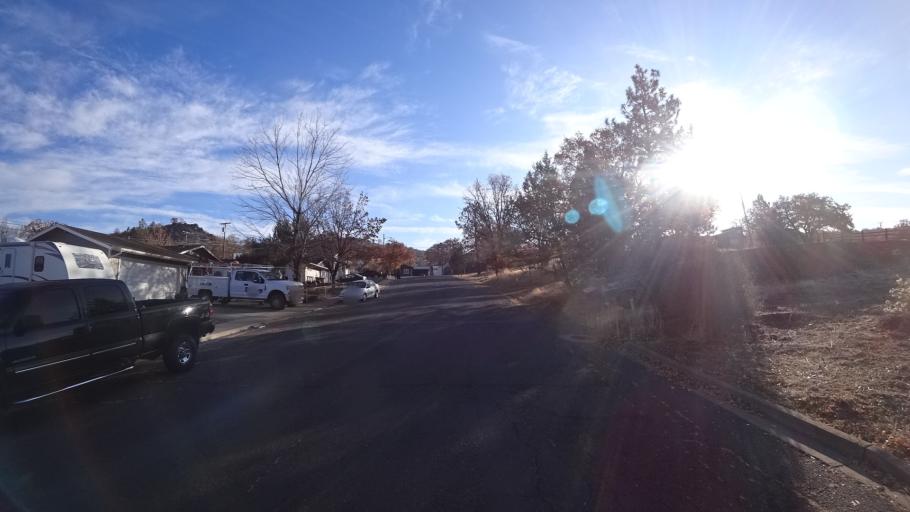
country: US
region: California
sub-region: Siskiyou County
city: Yreka
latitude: 41.7069
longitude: -122.6180
